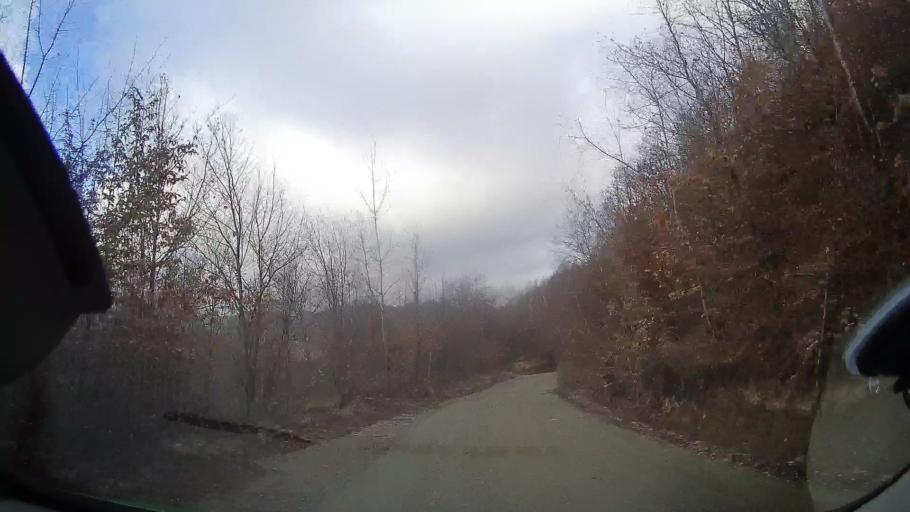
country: RO
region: Cluj
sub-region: Comuna Valea Ierii
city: Valea Ierii
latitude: 46.6775
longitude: 23.3140
